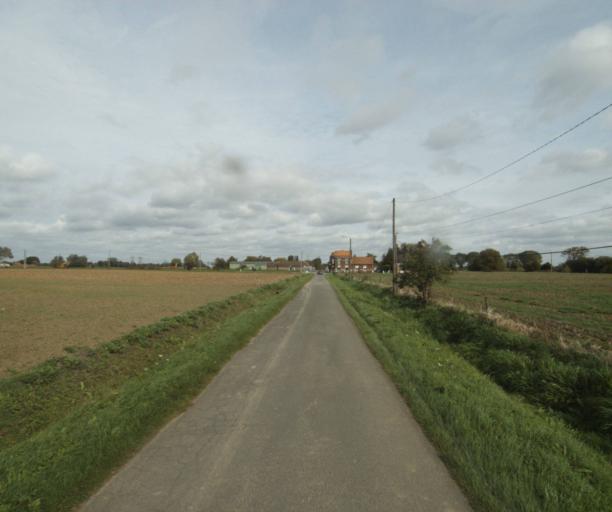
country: FR
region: Nord-Pas-de-Calais
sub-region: Departement du Nord
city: Bois-Grenier
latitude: 50.6343
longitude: 2.8897
